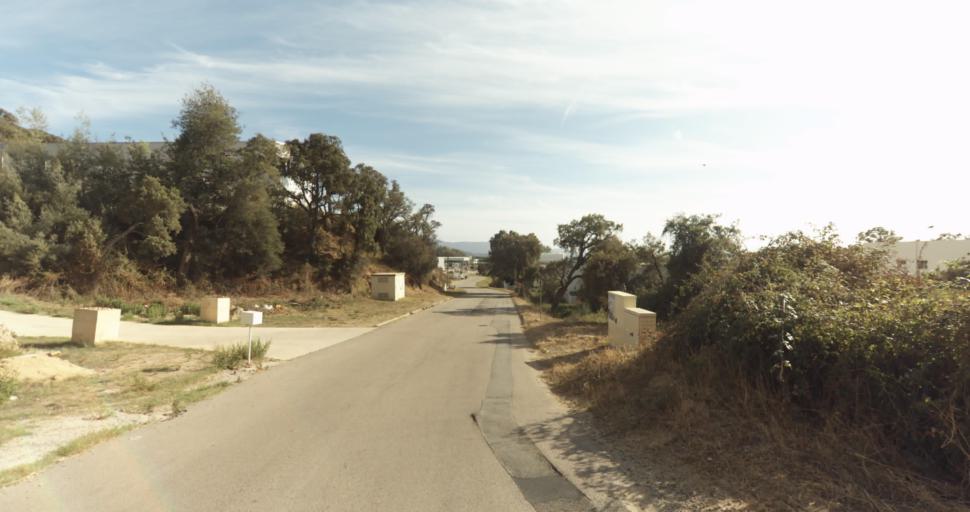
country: FR
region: Corsica
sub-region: Departement de la Corse-du-Sud
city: Afa
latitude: 41.9331
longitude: 8.7909
